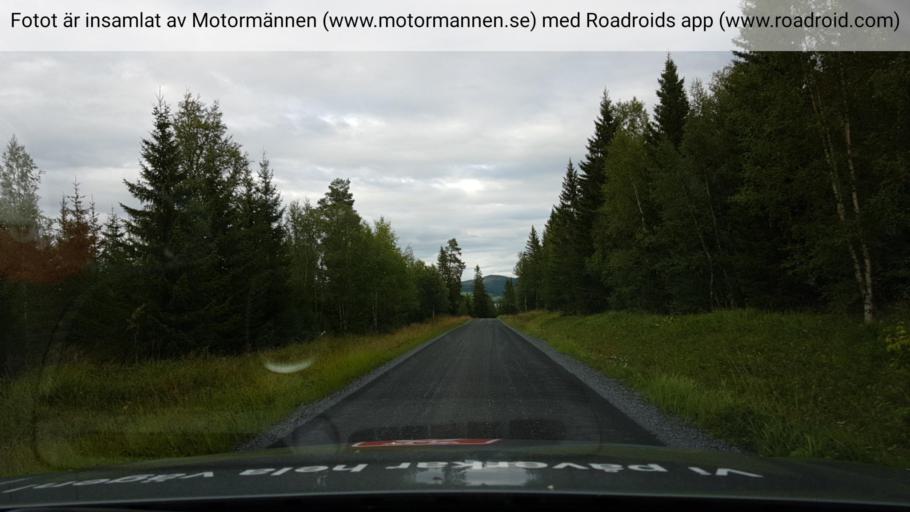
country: SE
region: Jaemtland
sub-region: Krokoms Kommun
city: Valla
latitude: 63.3648
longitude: 13.8992
